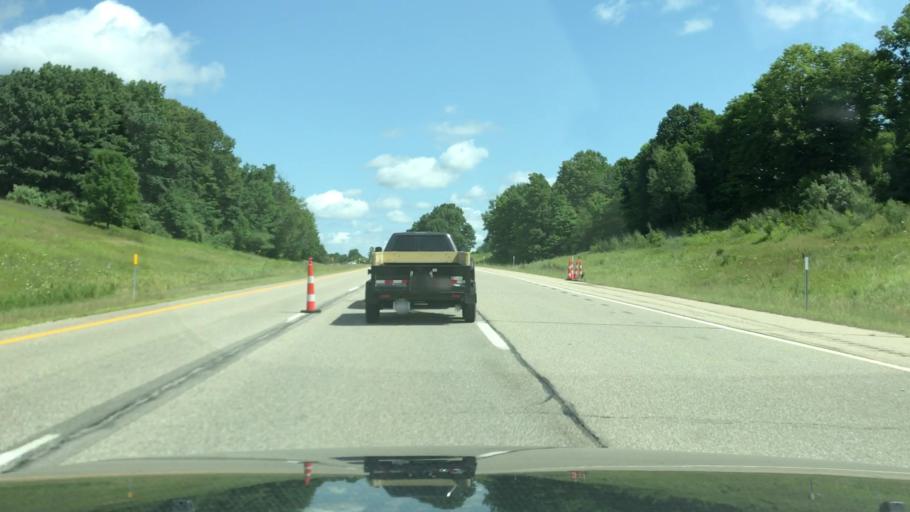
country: US
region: Michigan
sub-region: Mecosta County
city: Big Rapids
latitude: 43.7484
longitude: -85.5291
